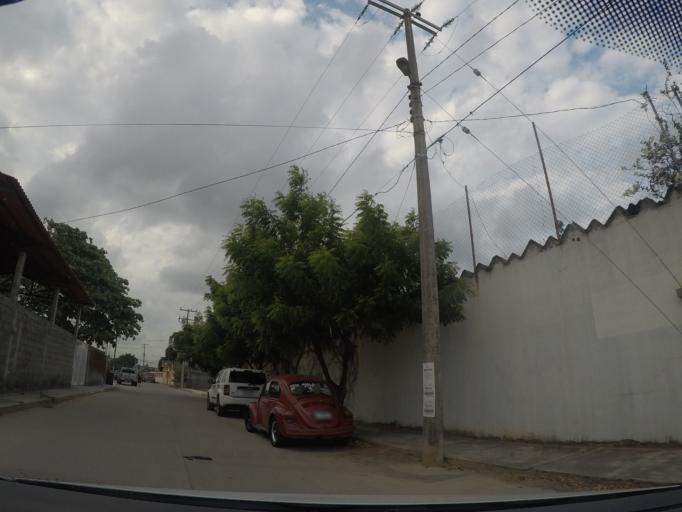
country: MX
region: Oaxaca
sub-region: Salina Cruz
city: Salina Cruz
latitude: 16.2130
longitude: -95.1949
